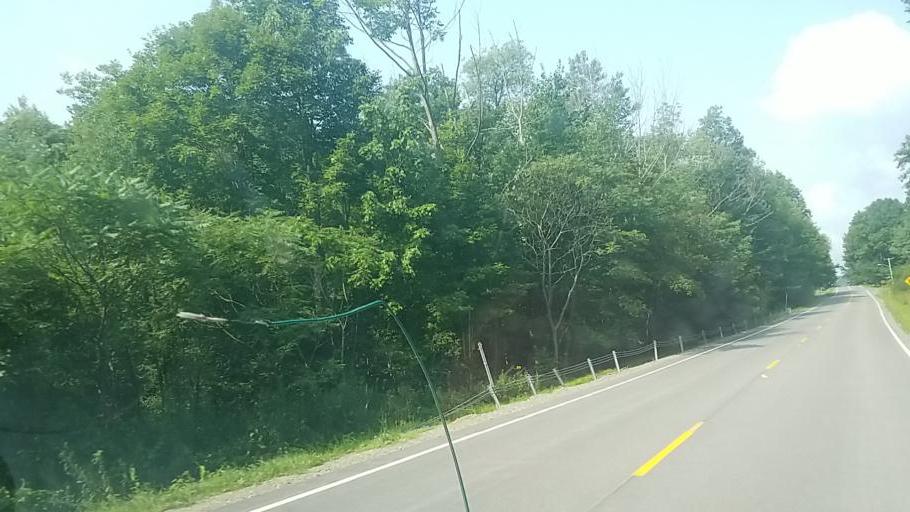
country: US
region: New York
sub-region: Fulton County
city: Gloversville
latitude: 43.1025
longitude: -74.3042
